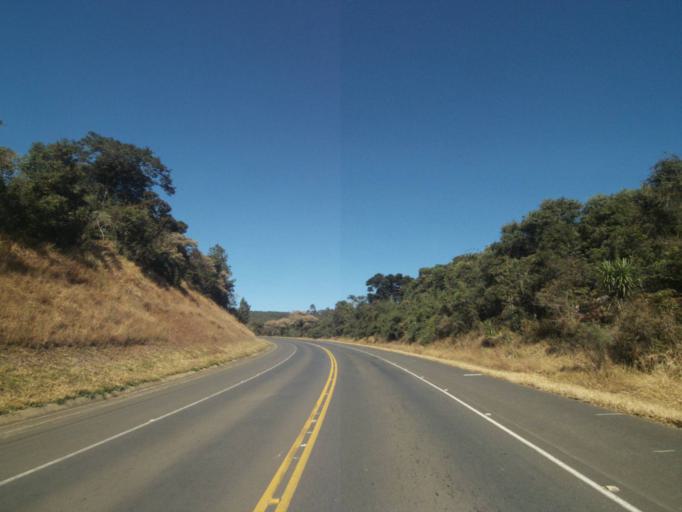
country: BR
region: Parana
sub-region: Tibagi
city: Tibagi
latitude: -24.5528
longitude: -50.4564
